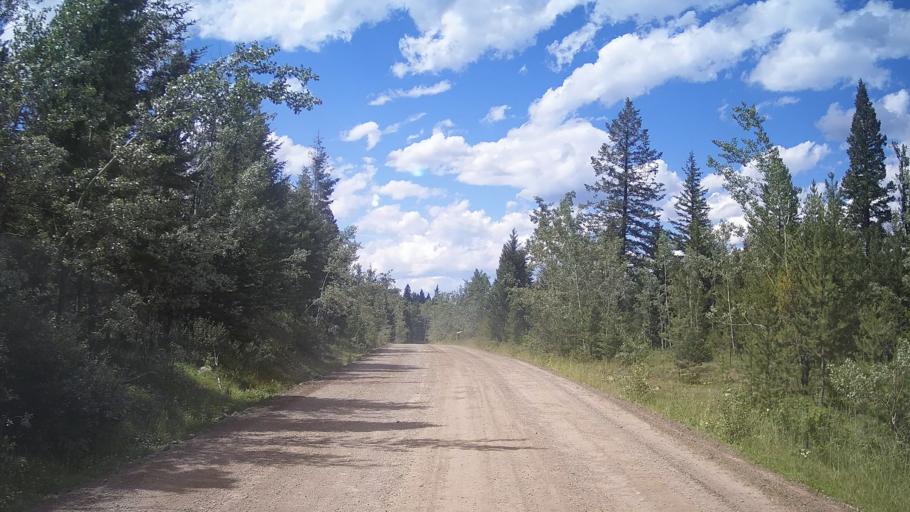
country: CA
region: British Columbia
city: Lillooet
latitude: 51.3283
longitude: -121.8877
